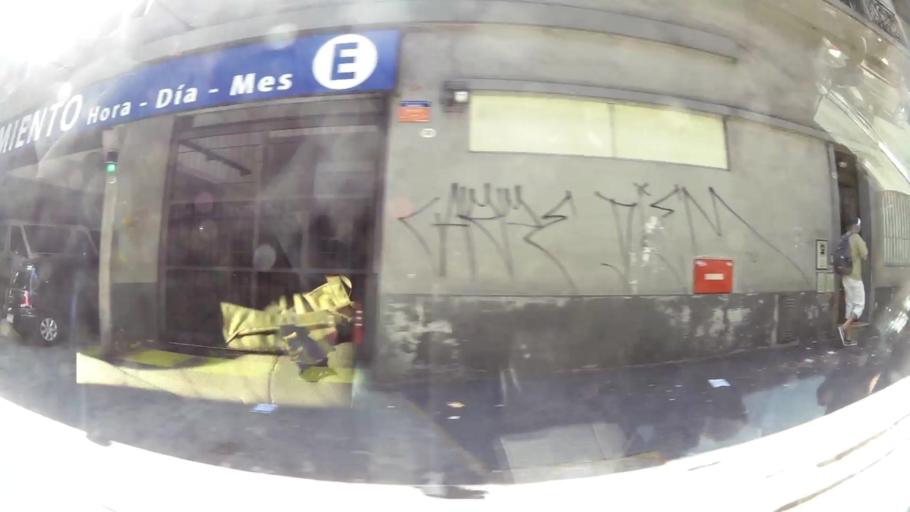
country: AR
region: Buenos Aires F.D.
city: Buenos Aires
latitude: -34.6115
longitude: -58.4095
